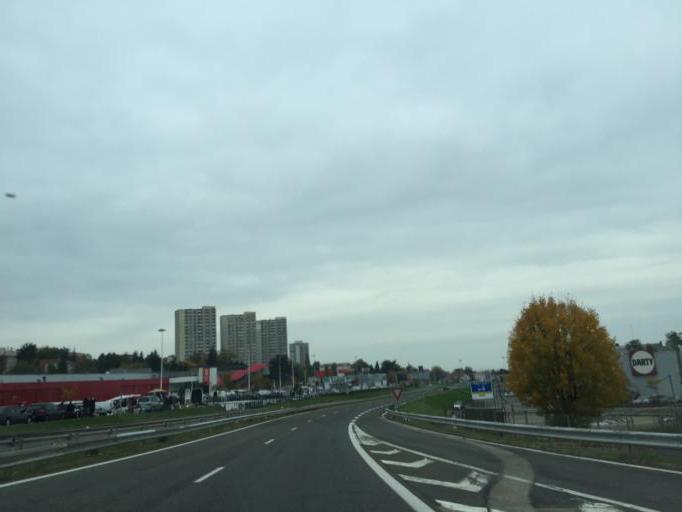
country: FR
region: Rhone-Alpes
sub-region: Departement de la Loire
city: Saint-Jean-Bonnefonds
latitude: 45.4413
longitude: 4.4236
